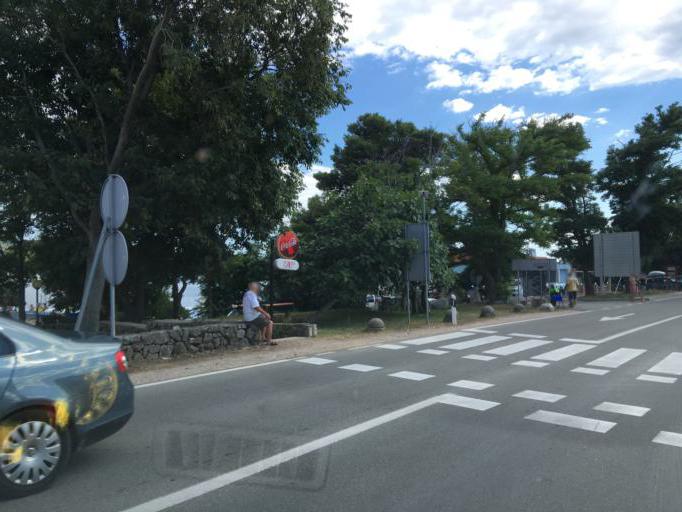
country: HR
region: Primorsko-Goranska
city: Punat
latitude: 45.0401
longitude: 14.6199
